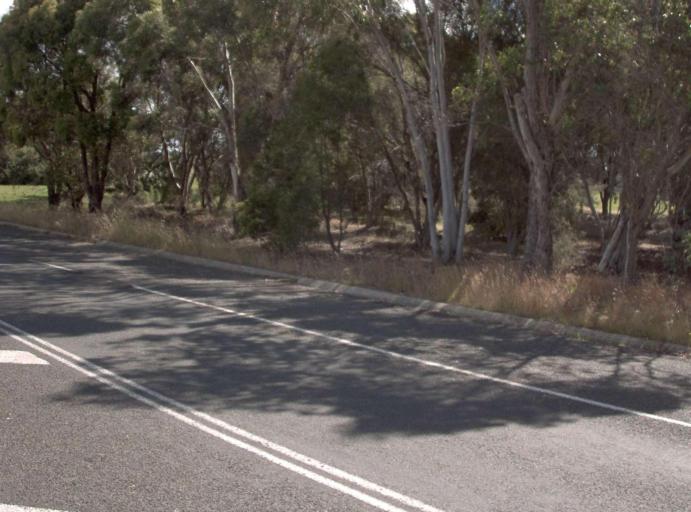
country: AU
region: Victoria
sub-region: Latrobe
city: Morwell
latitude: -38.2804
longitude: 146.4317
